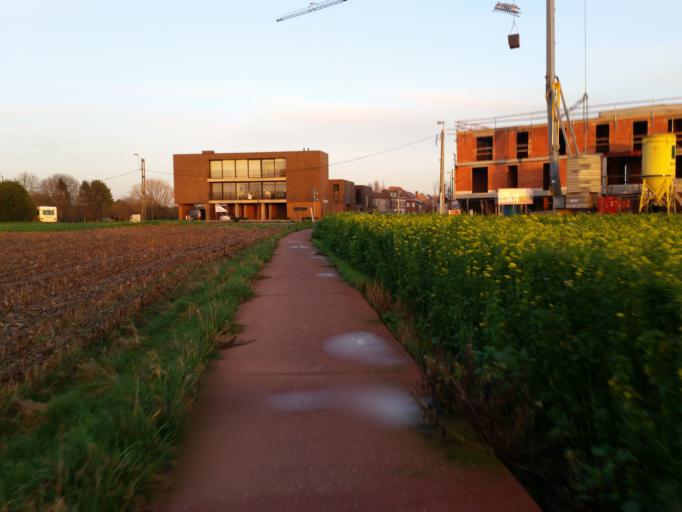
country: BE
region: Flanders
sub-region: Provincie Vlaams-Brabant
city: Machelen
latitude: 50.9295
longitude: 4.4515
